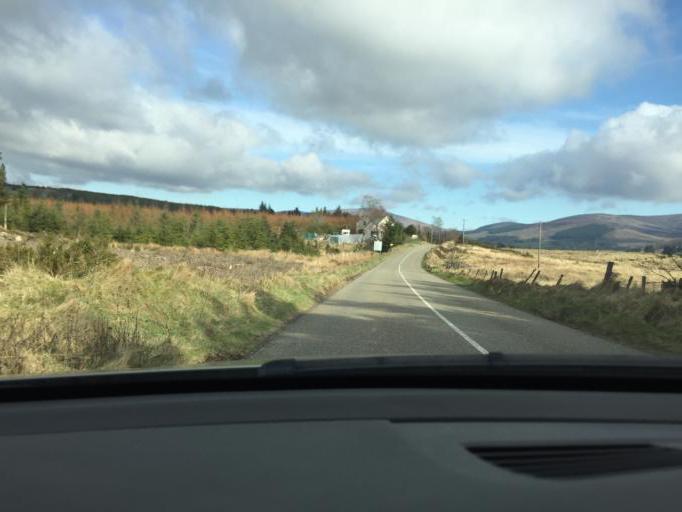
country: IE
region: Leinster
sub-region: Wicklow
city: Valleymount
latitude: 53.0644
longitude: -6.5207
